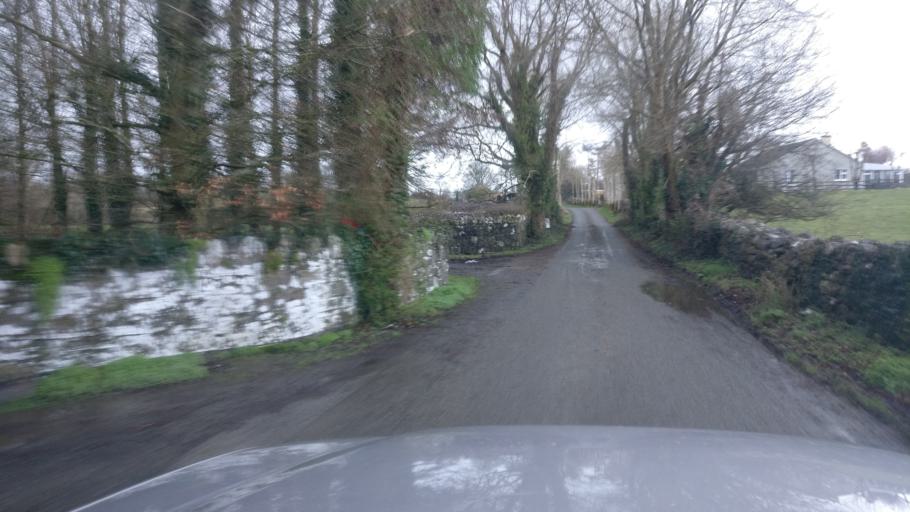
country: IE
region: Connaught
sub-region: County Galway
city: Loughrea
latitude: 53.1860
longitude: -8.6645
